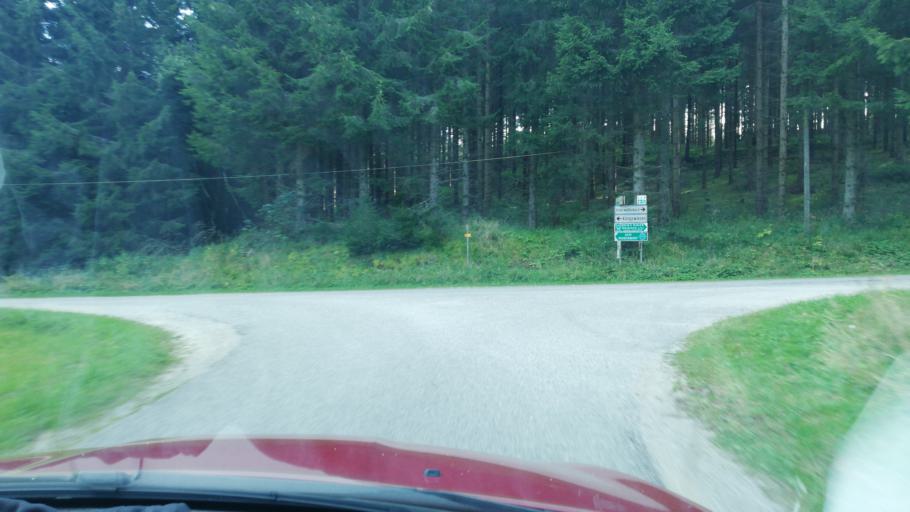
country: AT
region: Lower Austria
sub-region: Politischer Bezirk Zwettl
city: Langschlag
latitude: 48.4741
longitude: 14.8404
